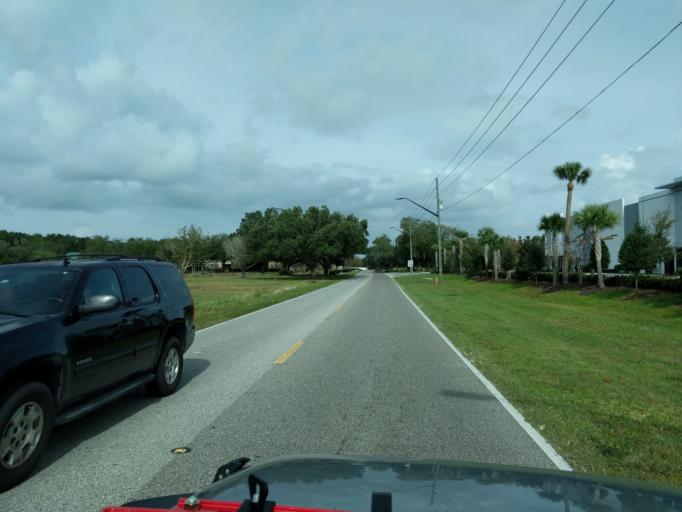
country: US
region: Florida
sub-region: Orange County
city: Ocoee
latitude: 28.5806
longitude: -81.5609
